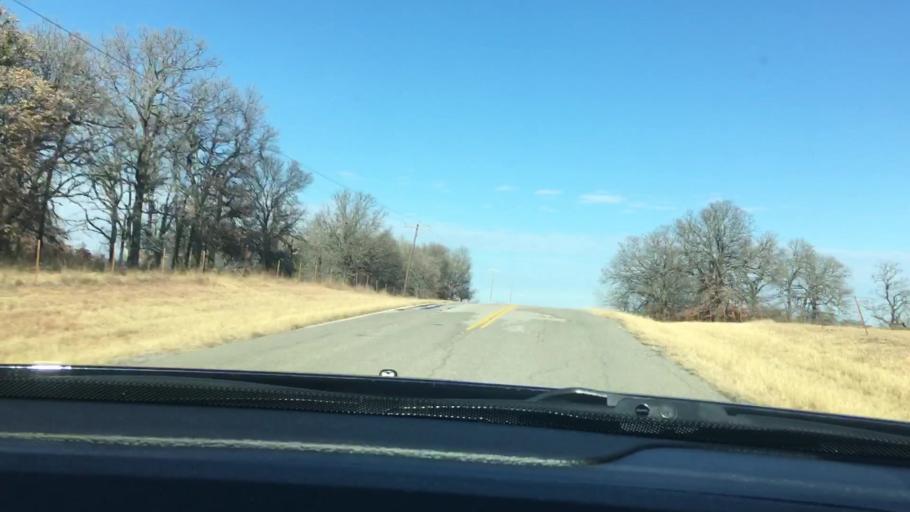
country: US
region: Oklahoma
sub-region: Garvin County
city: Wynnewood
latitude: 34.6701
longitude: -97.1254
